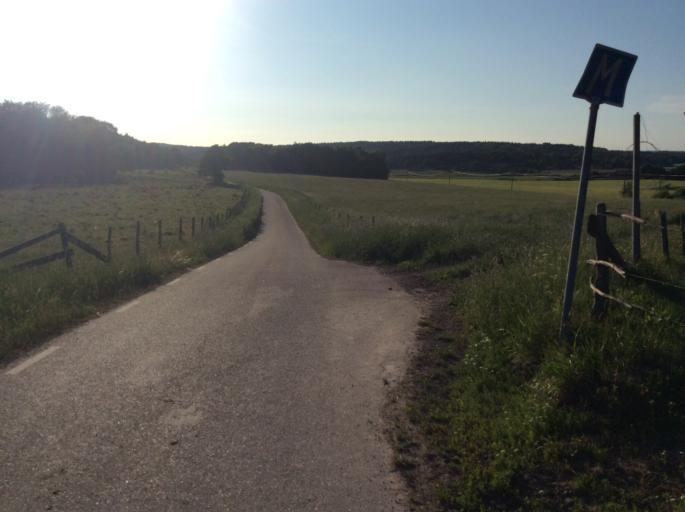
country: SE
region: Vaestra Goetaland
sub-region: Goteborg
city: Majorna
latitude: 57.7947
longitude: 11.8690
